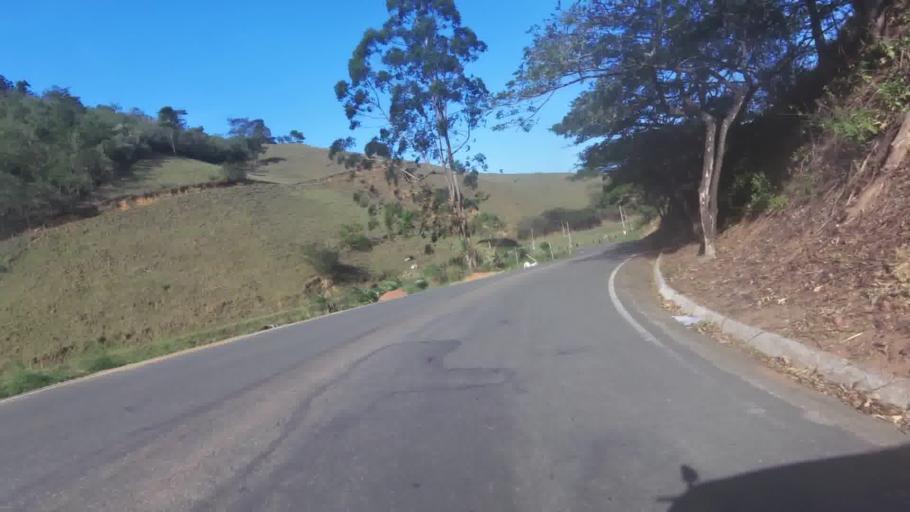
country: BR
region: Espirito Santo
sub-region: Iconha
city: Iconha
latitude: -20.7310
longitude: -40.7735
